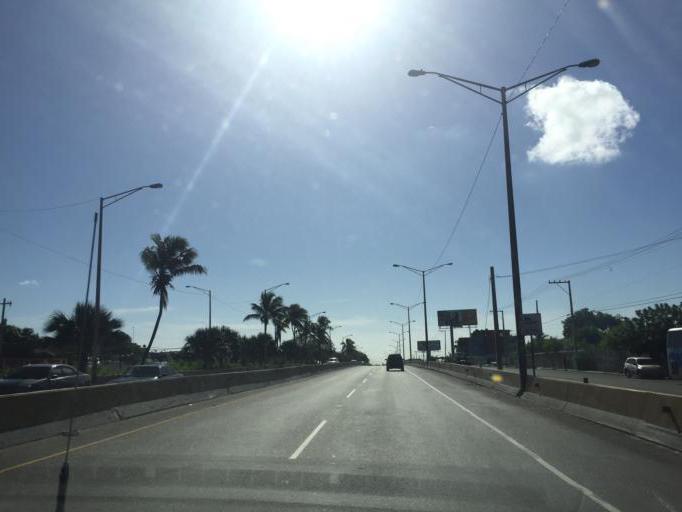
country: DO
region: Santo Domingo
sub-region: Santo Domingo
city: Santo Domingo Este
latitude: 18.4800
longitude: -69.8380
